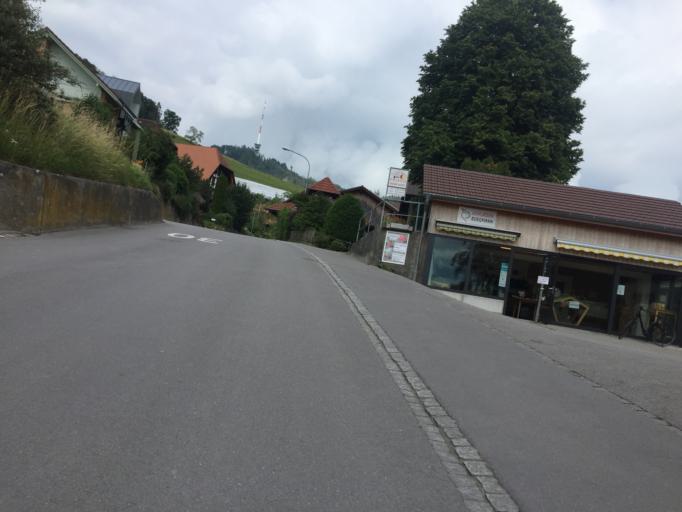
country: CH
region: Bern
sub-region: Bern-Mittelland District
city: Bolligen
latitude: 46.9741
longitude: 7.5070
